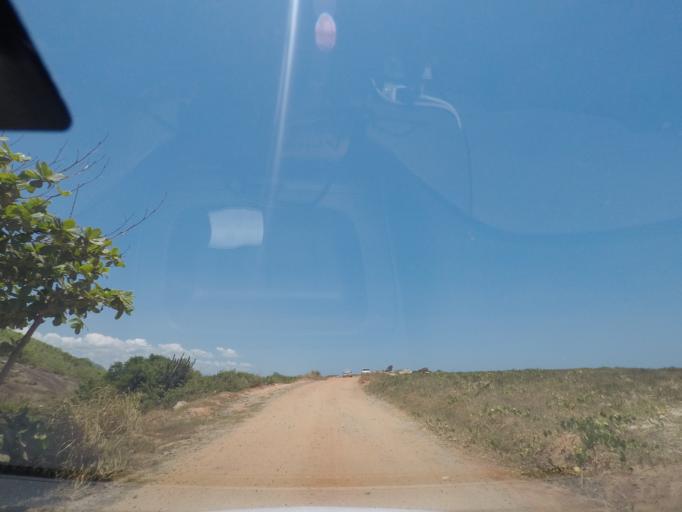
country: BR
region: Rio de Janeiro
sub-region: Niteroi
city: Niteroi
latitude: -22.9690
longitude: -43.0014
